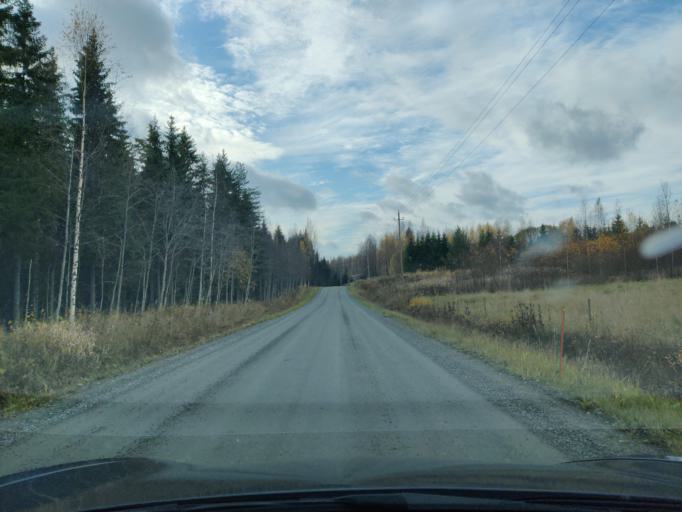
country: FI
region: Northern Savo
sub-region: Kuopio
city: Siilinjaervi
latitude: 63.1198
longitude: 27.5470
